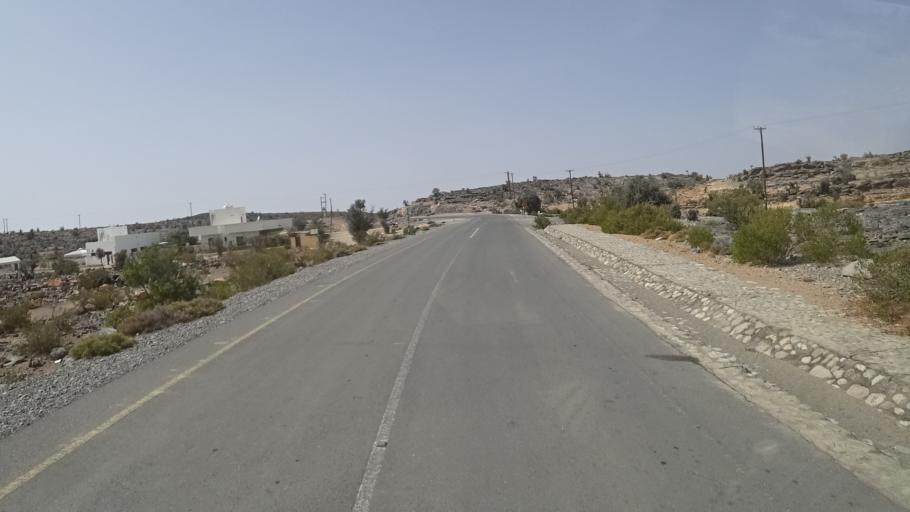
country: OM
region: Al Batinah
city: Bayt al `Awabi
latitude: 23.1522
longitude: 57.4232
